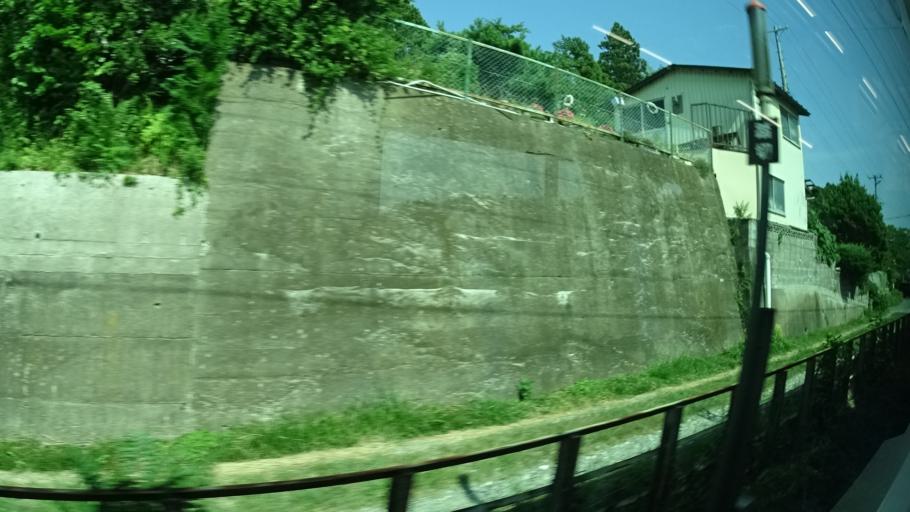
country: JP
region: Miyagi
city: Kogota
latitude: 38.5000
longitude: 141.0844
